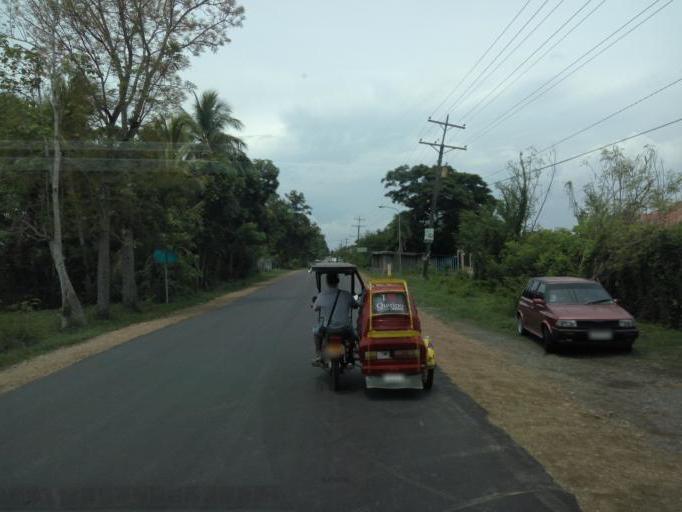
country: PH
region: Cagayan Valley
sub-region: Province of Quirino
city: Saguday
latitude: 16.5138
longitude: 121.5424
